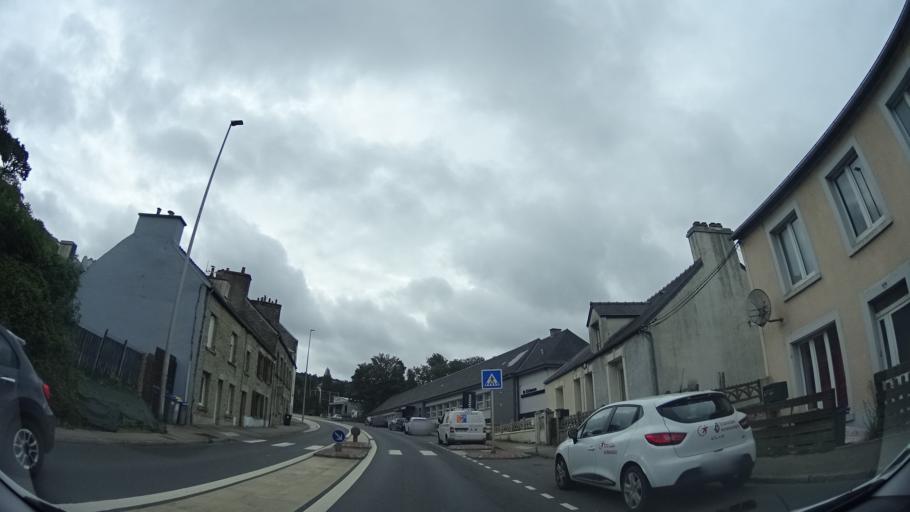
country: FR
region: Lower Normandy
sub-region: Departement de la Manche
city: Cherbourg-Octeville
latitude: 49.6243
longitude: -1.6162
